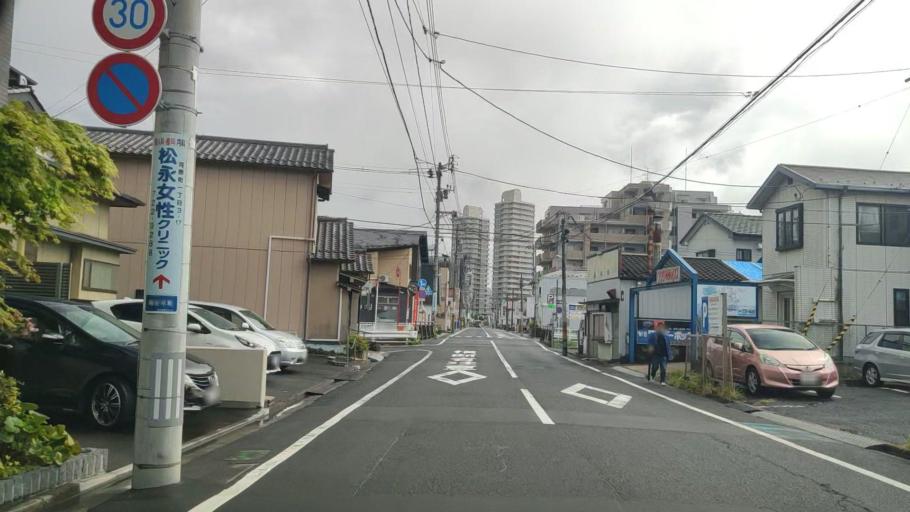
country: JP
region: Miyagi
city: Sendai
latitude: 38.2437
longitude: 140.8892
